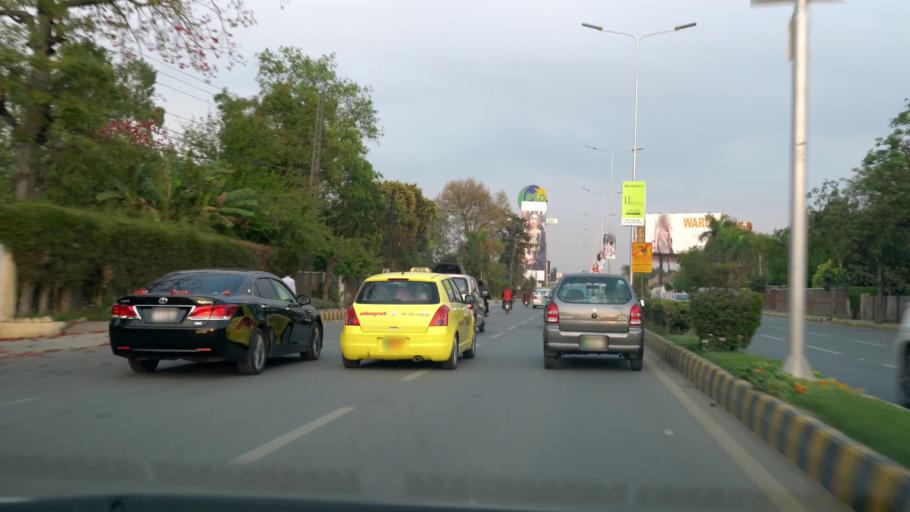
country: PK
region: Punjab
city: Lahore
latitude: 31.5018
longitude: 74.3623
